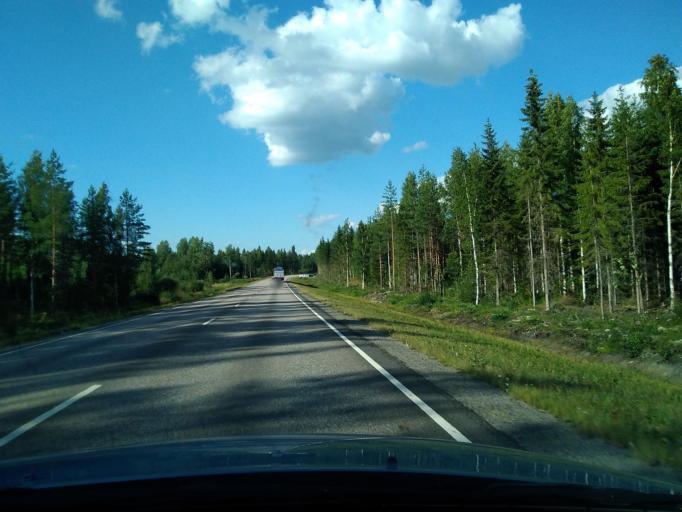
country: FI
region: Central Finland
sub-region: Keuruu
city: Keuruu
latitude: 62.1553
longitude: 24.7503
